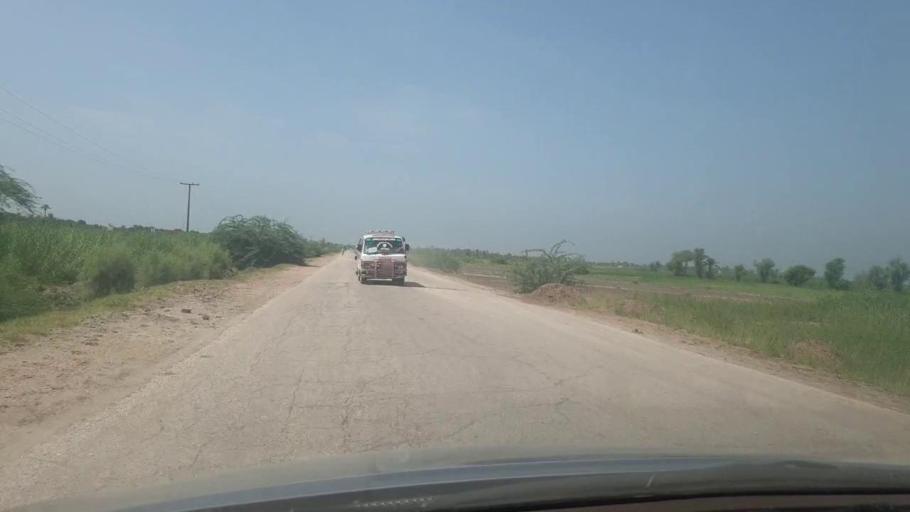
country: PK
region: Sindh
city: Ranipur
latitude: 27.2654
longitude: 68.5922
